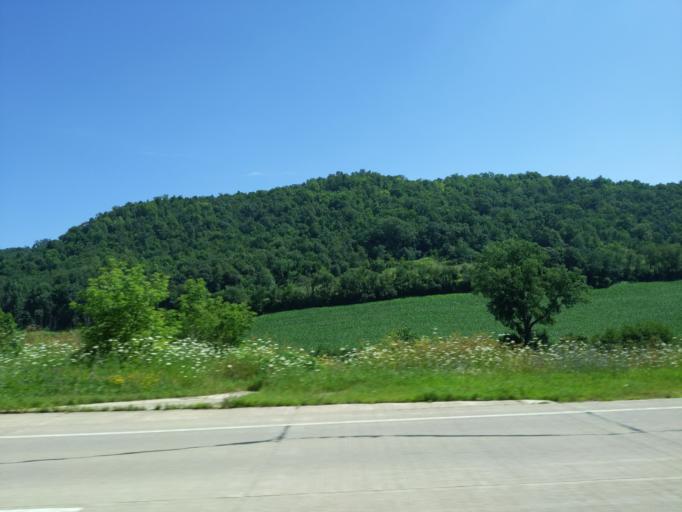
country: US
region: Wisconsin
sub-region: La Crosse County
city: Bangor
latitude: 43.7041
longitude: -91.0457
